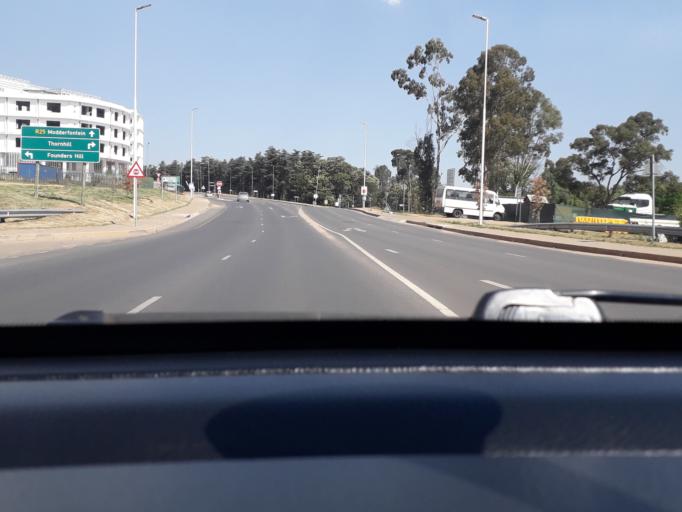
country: ZA
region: Gauteng
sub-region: City of Johannesburg Metropolitan Municipality
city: Modderfontein
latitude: -26.0988
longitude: 28.1581
